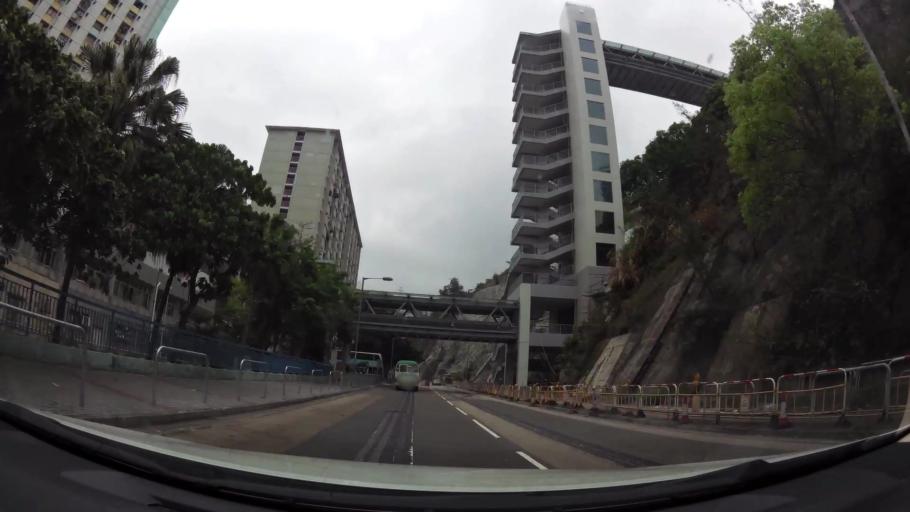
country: HK
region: Kowloon City
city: Kowloon
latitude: 22.3291
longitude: 114.2271
